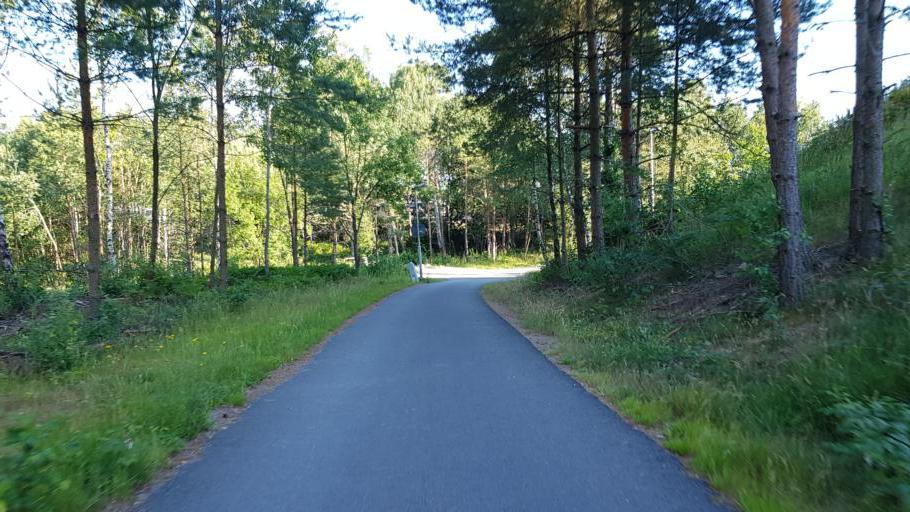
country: SE
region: Vaestra Goetaland
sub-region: Harryda Kommun
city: Molnlycke
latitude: 57.6724
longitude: 12.0976
